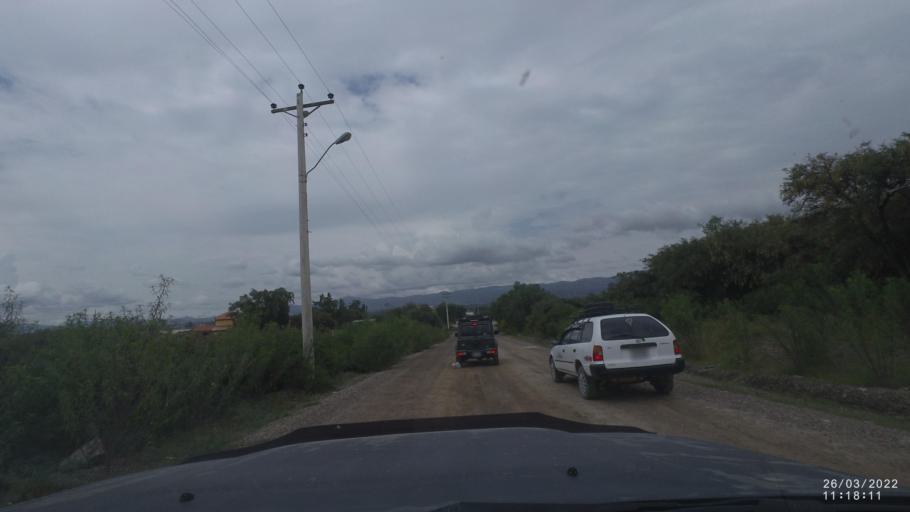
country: BO
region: Cochabamba
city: Tarata
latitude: -17.5428
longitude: -66.0226
